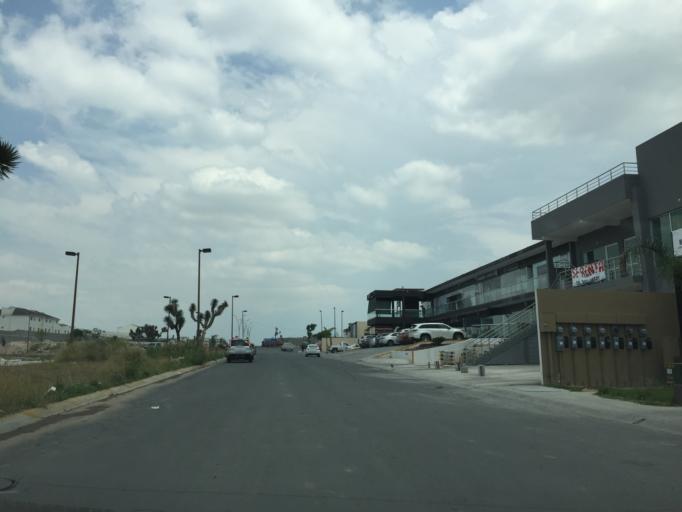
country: MX
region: Nuevo Leon
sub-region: Garcia
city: Mitras Poniente
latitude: 25.7491
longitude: -100.4200
